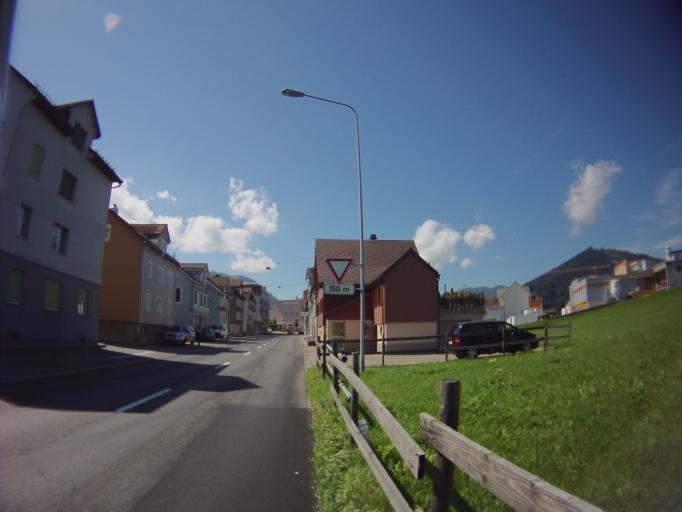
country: CH
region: Schwyz
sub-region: Bezirk Einsiedeln
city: Einsiedeln
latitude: 47.1297
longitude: 8.7436
